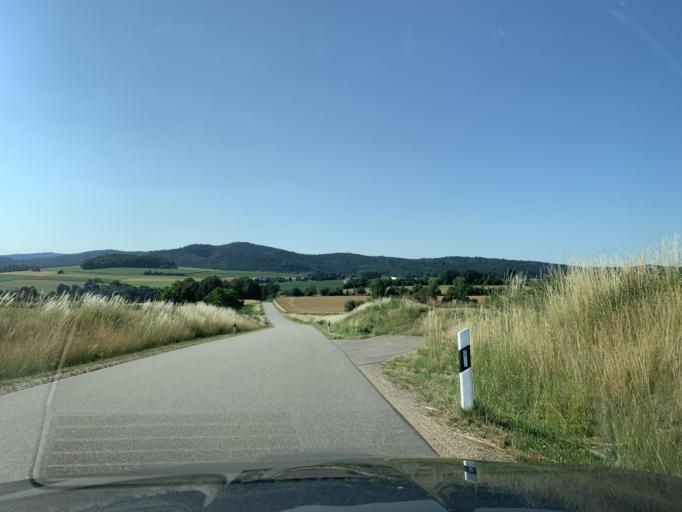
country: DE
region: Bavaria
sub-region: Upper Palatinate
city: Dieterskirchen
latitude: 49.4121
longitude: 12.4129
